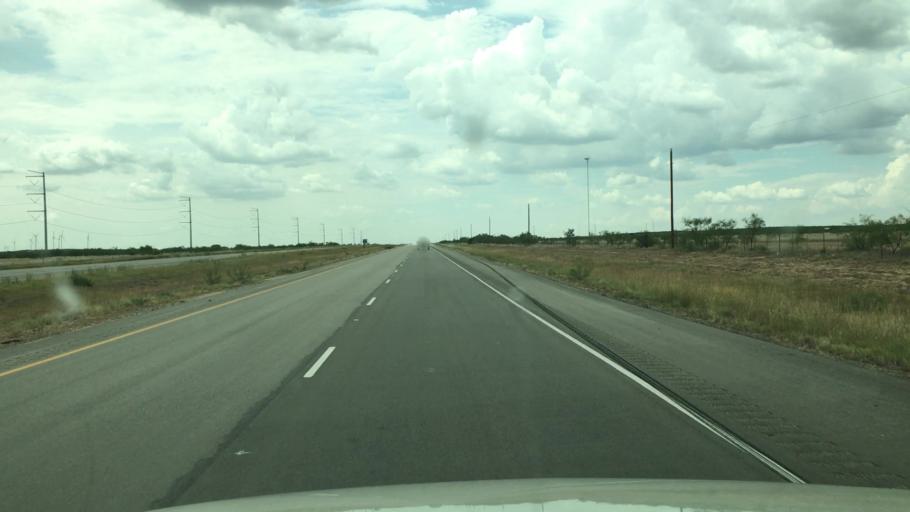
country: US
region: Texas
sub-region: Glasscock County
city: Garden City
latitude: 31.9746
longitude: -101.2468
